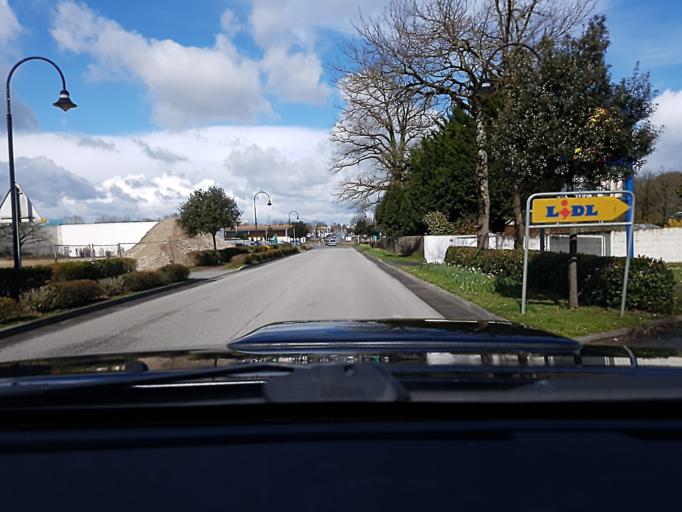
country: FR
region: Pays de la Loire
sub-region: Departement de la Vendee
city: Aizenay
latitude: 46.7337
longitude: -1.5909
